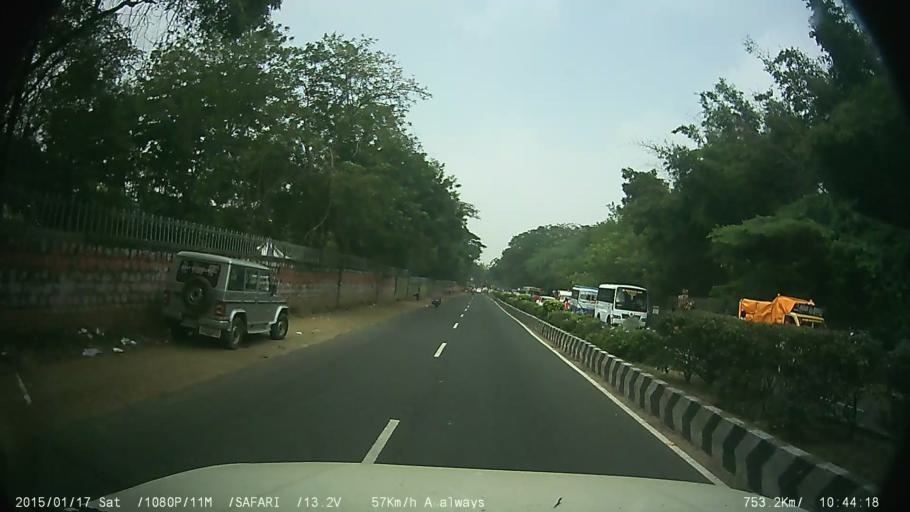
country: IN
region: Tamil Nadu
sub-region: Kancheepuram
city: Vandalur
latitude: 12.8782
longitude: 80.0828
